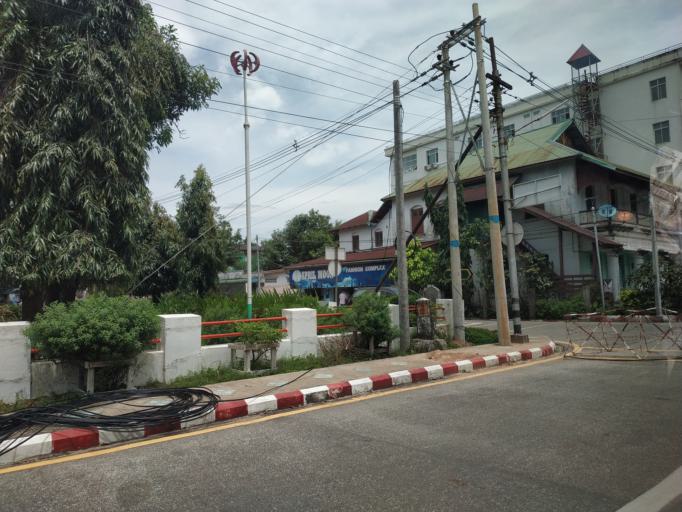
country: MM
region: Tanintharyi
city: Dawei
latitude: 14.0731
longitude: 98.1935
